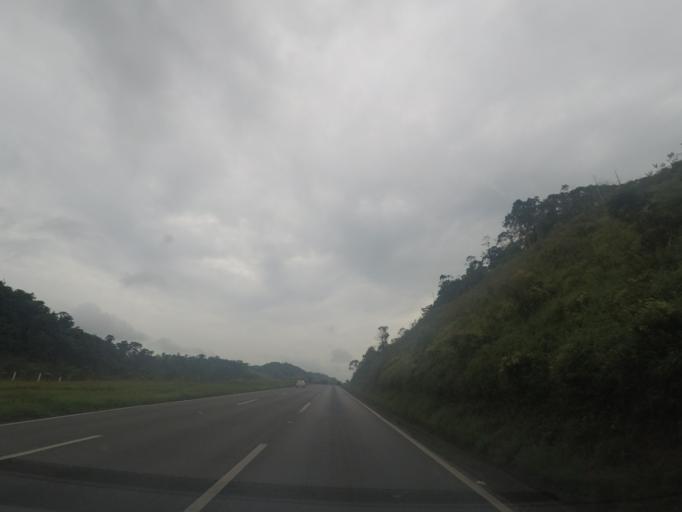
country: BR
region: Sao Paulo
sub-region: Cajati
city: Cajati
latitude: -24.8974
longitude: -48.2462
